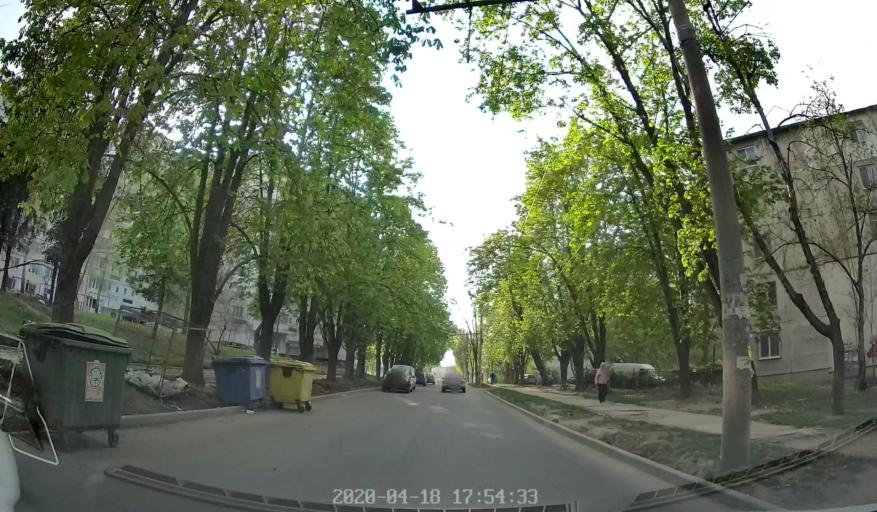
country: MD
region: Chisinau
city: Chisinau
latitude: 46.9936
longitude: 28.8493
